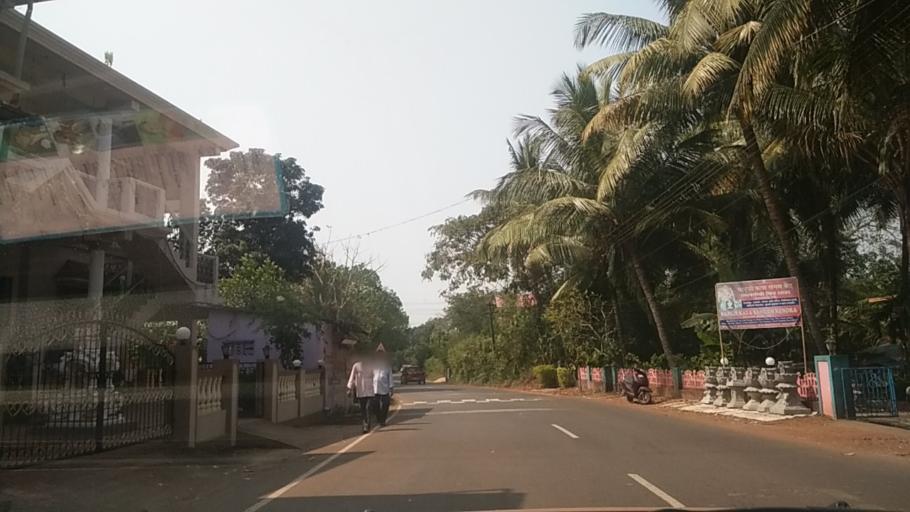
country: IN
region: Goa
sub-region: North Goa
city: Morjim
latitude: 15.6619
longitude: 73.7338
